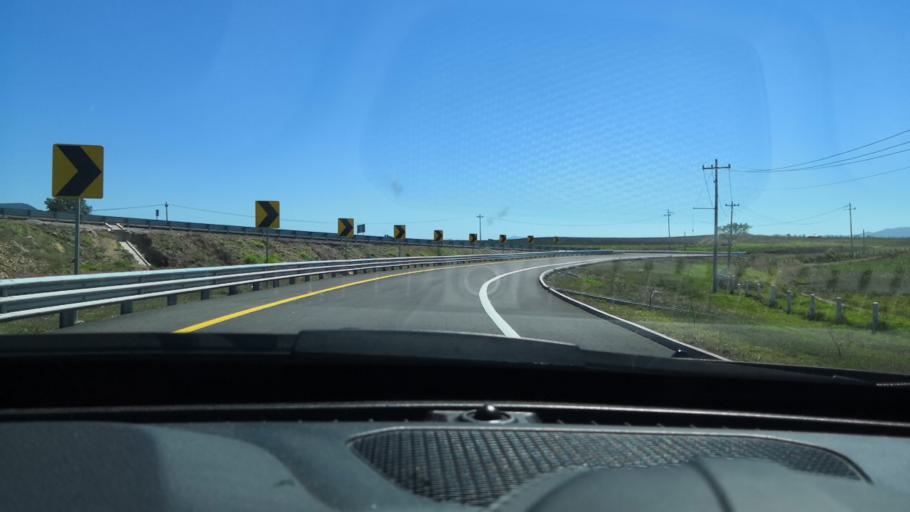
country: MX
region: Nayarit
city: Compostela
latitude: 21.2300
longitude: -104.8738
